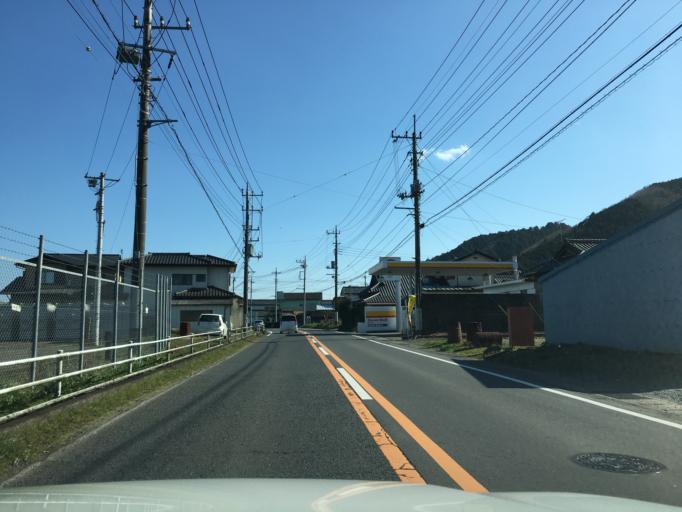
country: JP
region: Ibaraki
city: Omiya
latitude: 36.5422
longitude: 140.3365
